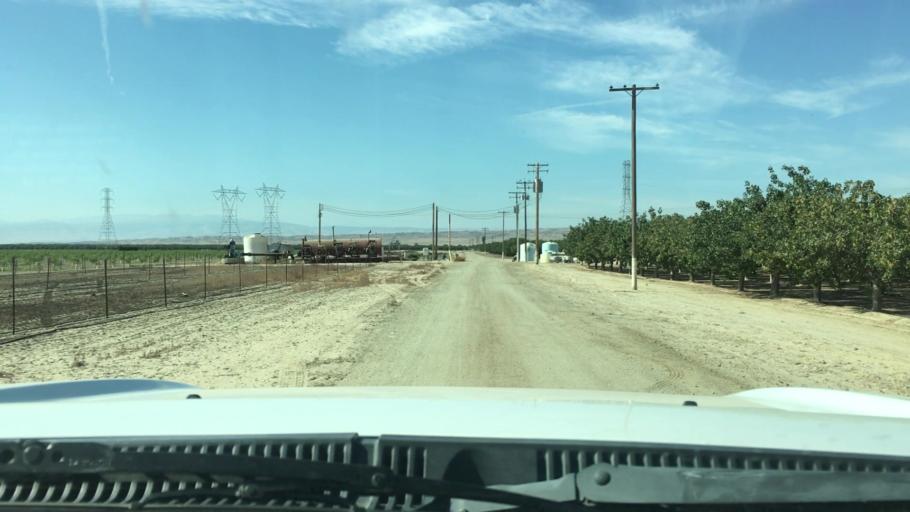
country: US
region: California
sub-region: Kern County
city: Buttonwillow
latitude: 35.3741
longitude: -119.3856
